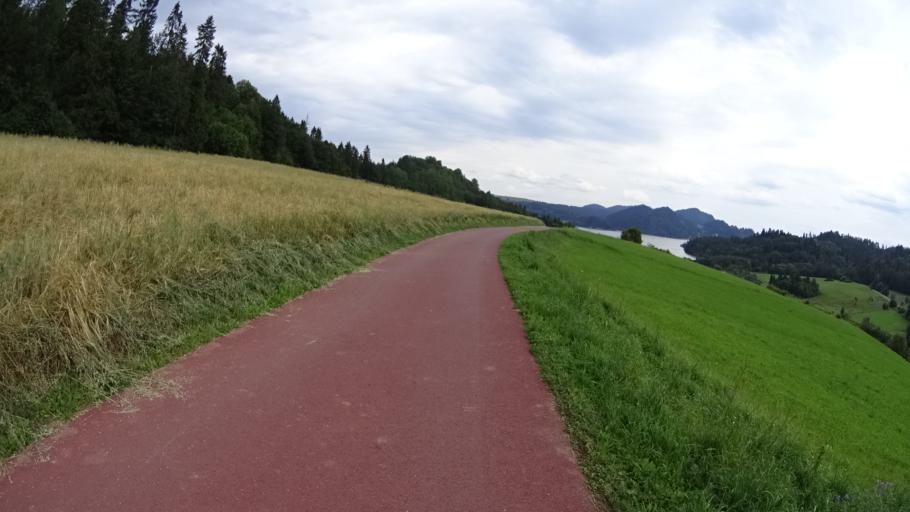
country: PL
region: Lesser Poland Voivodeship
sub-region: Powiat nowotarski
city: Niedzica
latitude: 49.4300
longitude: 20.2896
